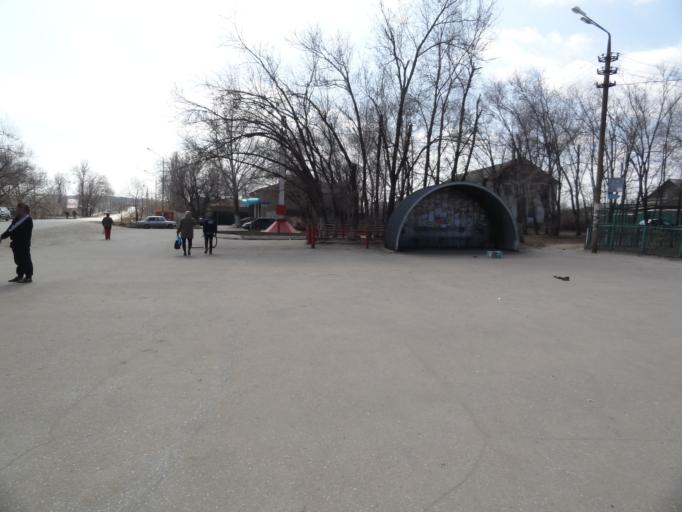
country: RU
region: Saratov
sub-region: Saratovskiy Rayon
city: Saratov
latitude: 51.6630
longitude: 46.0658
